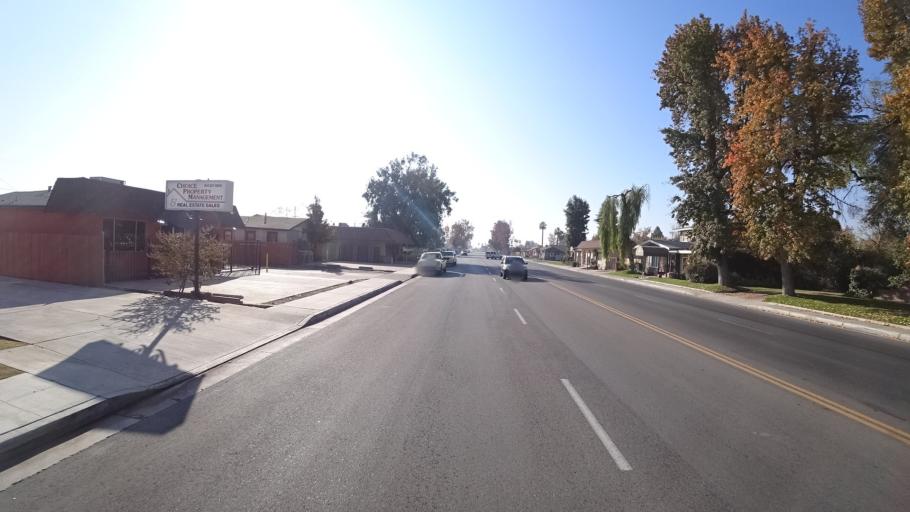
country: US
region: California
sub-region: Kern County
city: Bakersfield
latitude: 35.3578
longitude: -119.0213
